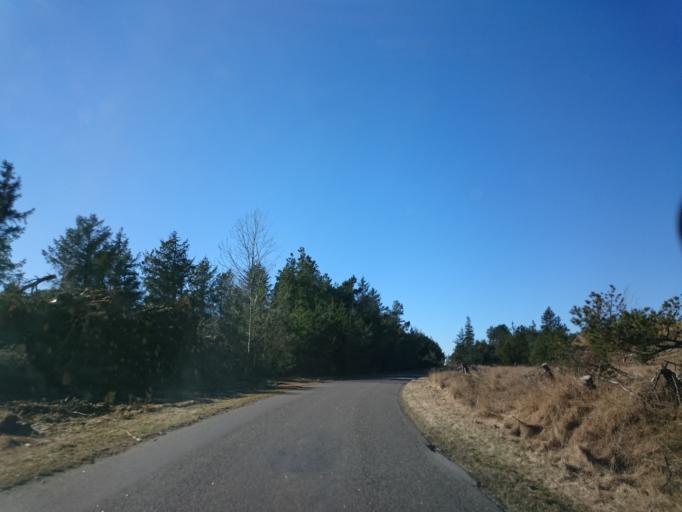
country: DK
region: North Denmark
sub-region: Hjorring Kommune
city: Sindal
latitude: 57.6172
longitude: 10.2943
